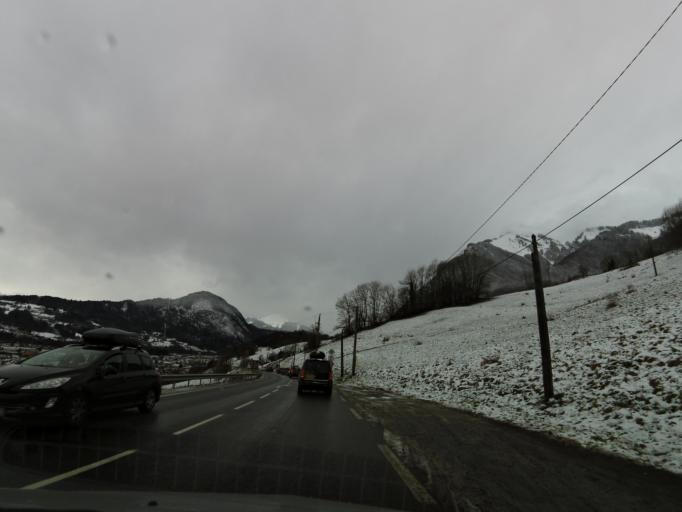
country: FR
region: Rhone-Alpes
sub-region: Departement de la Haute-Savoie
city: Taninges
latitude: 46.1102
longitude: 6.6094
